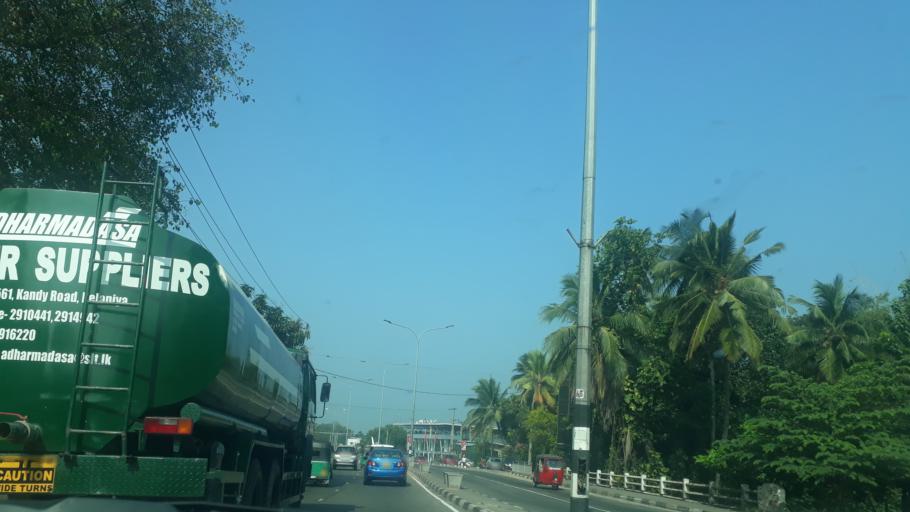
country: LK
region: Western
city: Wattala
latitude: 6.9678
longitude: 79.9035
